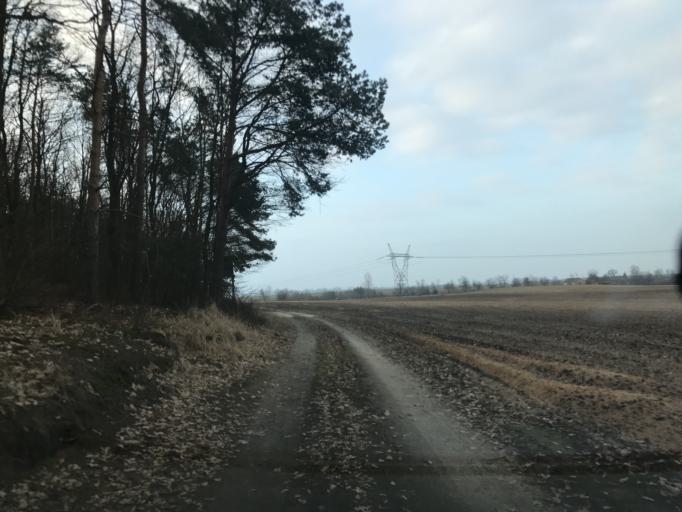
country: PL
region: Kujawsko-Pomorskie
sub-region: Powiat golubsko-dobrzynski
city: Golub-Dobrzyn
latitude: 53.1805
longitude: 18.9995
